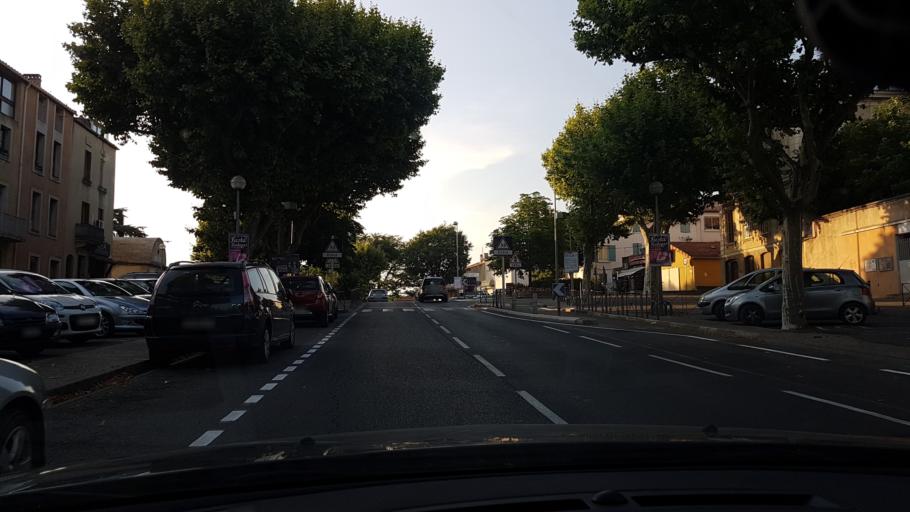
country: FR
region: Provence-Alpes-Cote d'Azur
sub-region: Departement du Vaucluse
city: Carpentras
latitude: 44.0565
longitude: 5.0513
